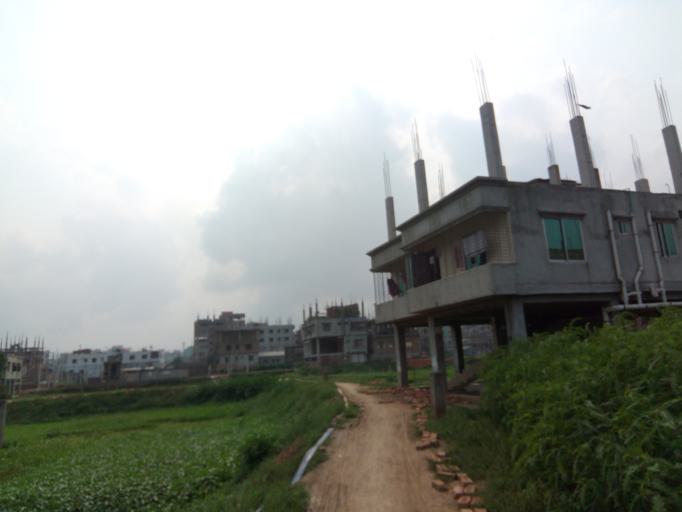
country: BD
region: Dhaka
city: Paltan
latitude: 23.7261
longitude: 90.4419
